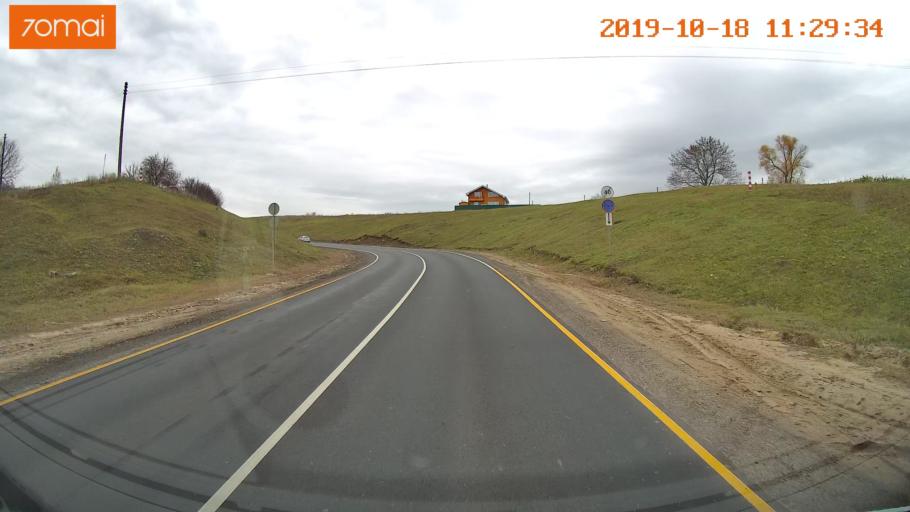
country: RU
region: Rjazan
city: Oktyabr'skiy
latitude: 54.1559
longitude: 38.6784
